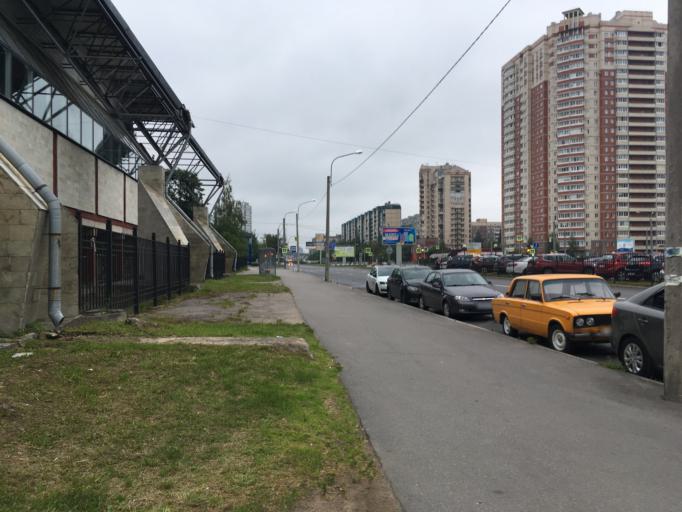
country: RU
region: St.-Petersburg
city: Komendantsky aerodrom
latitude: 60.0129
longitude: 30.2770
